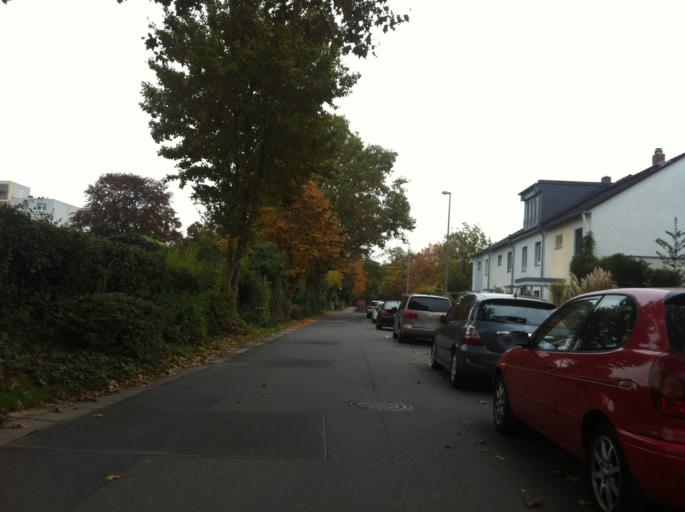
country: DE
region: Rheinland-Pfalz
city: Mainz
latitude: 49.9848
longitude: 8.2838
